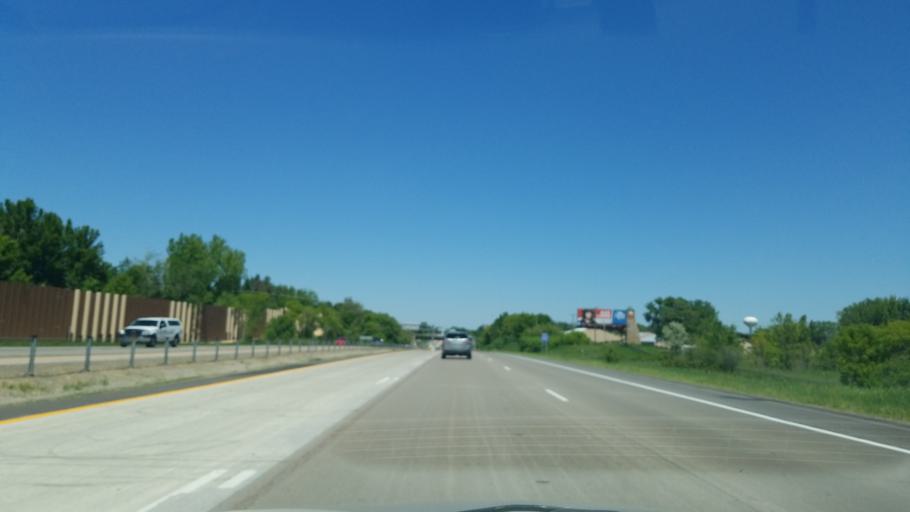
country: US
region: Minnesota
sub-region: Ramsey County
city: North Oaks
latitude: 45.0848
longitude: -93.0527
